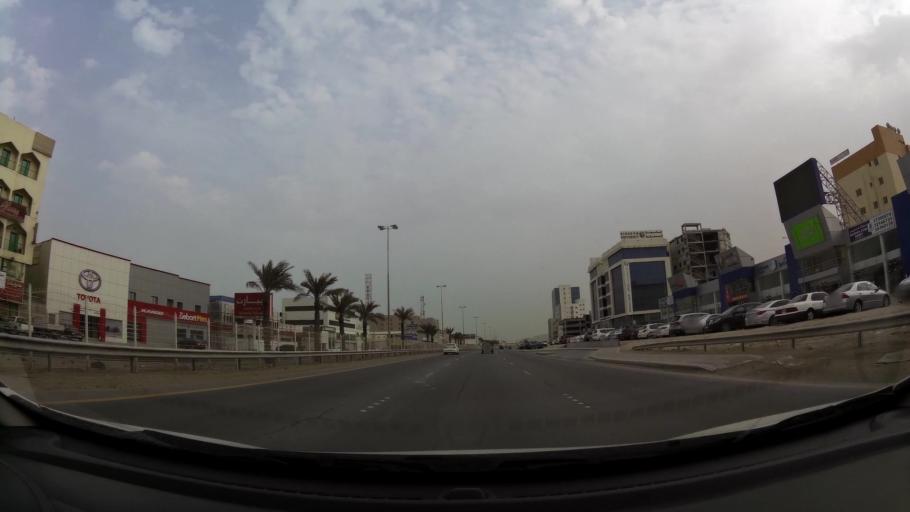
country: BH
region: Northern
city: Ar Rifa'
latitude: 26.1377
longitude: 50.5830
